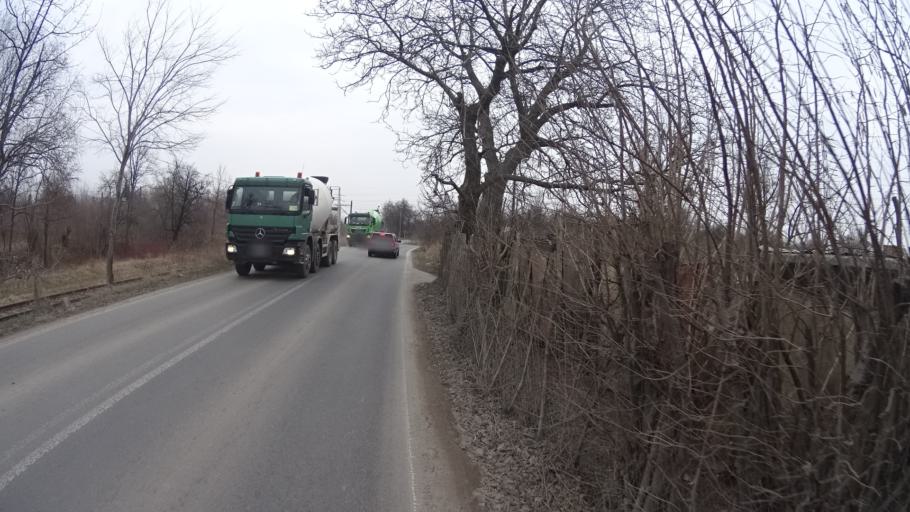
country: PL
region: Masovian Voivodeship
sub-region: Warszawa
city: Ochota
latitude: 52.2196
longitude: 20.9453
